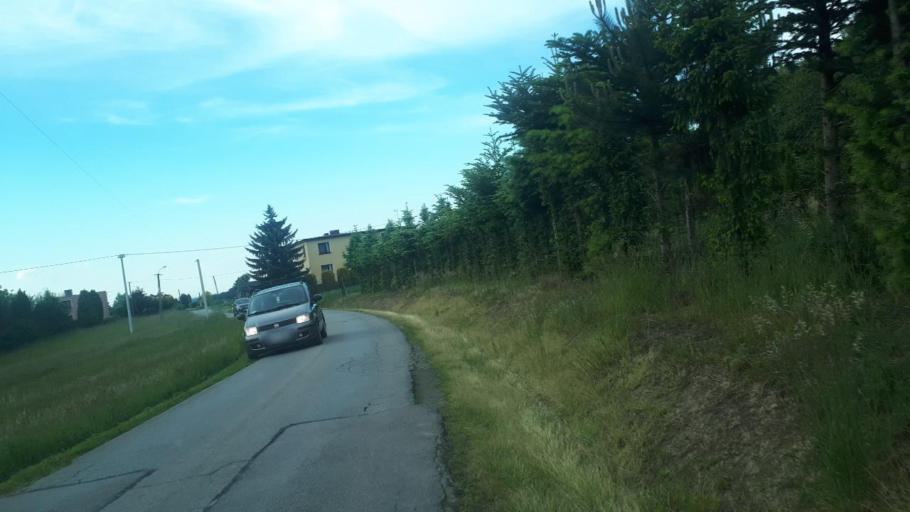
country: PL
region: Silesian Voivodeship
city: Janowice
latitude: 49.8850
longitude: 19.1019
